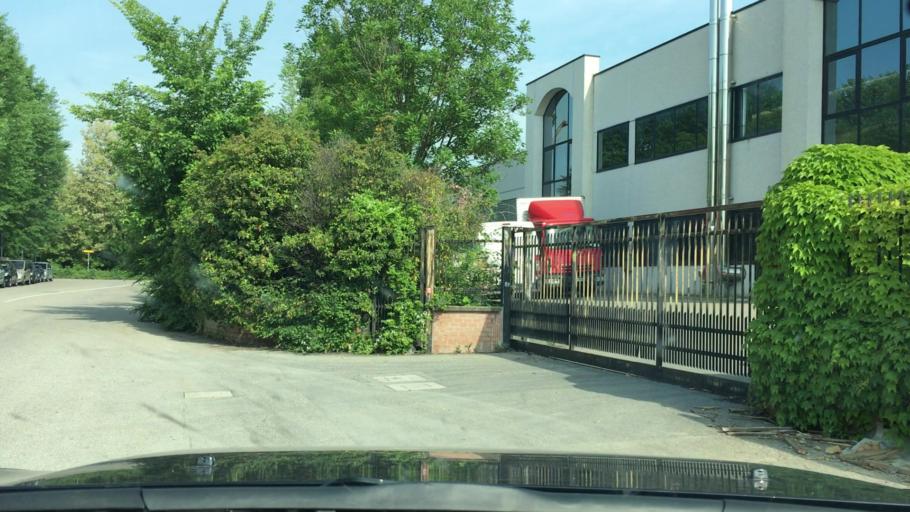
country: IT
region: Emilia-Romagna
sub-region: Provincia di Bologna
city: Quarto Inferiore
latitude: 44.5519
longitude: 11.3921
